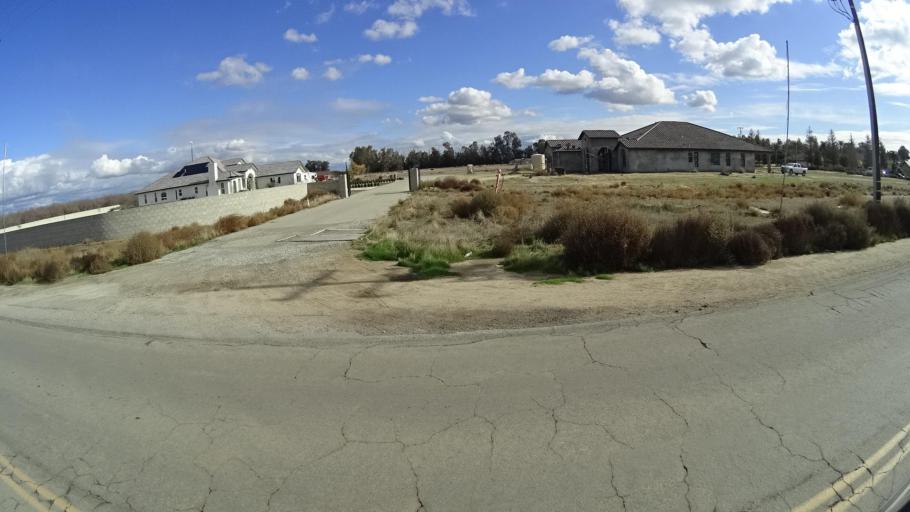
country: US
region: California
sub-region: Kern County
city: Greenfield
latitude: 35.2407
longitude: -119.0922
